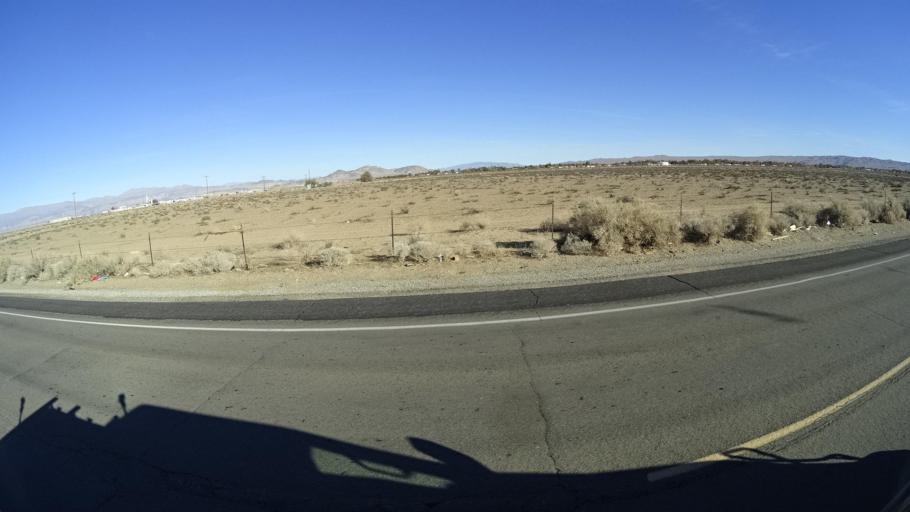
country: US
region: California
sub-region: Kern County
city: China Lake Acres
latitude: 35.6468
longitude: -117.7231
